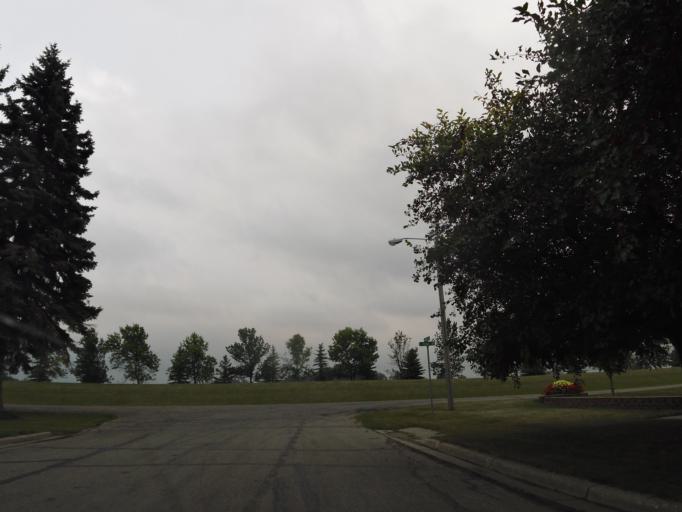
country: US
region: North Dakota
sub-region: Walsh County
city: Grafton
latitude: 48.5572
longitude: -97.1735
